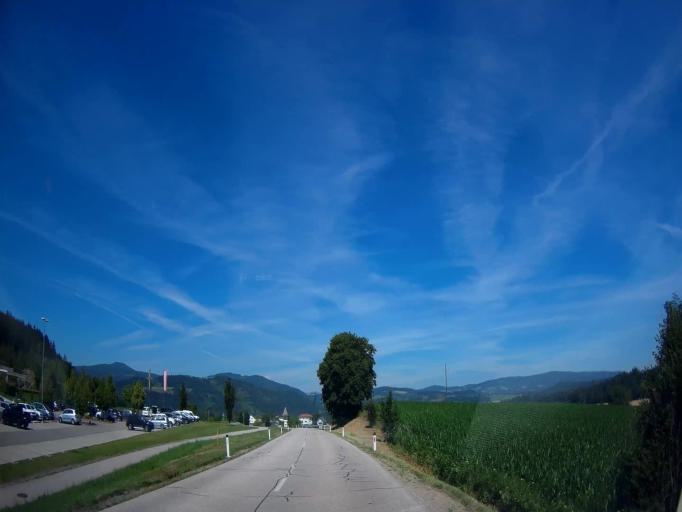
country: AT
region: Carinthia
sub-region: Politischer Bezirk Sankt Veit an der Glan
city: St. Georgen am Laengsee
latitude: 46.7963
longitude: 14.4165
